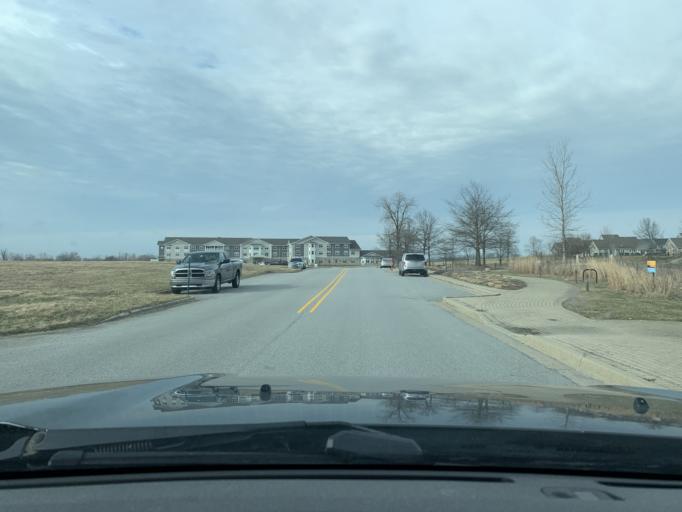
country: US
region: Indiana
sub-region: Porter County
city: Chesterton
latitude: 41.5833
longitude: -87.0421
